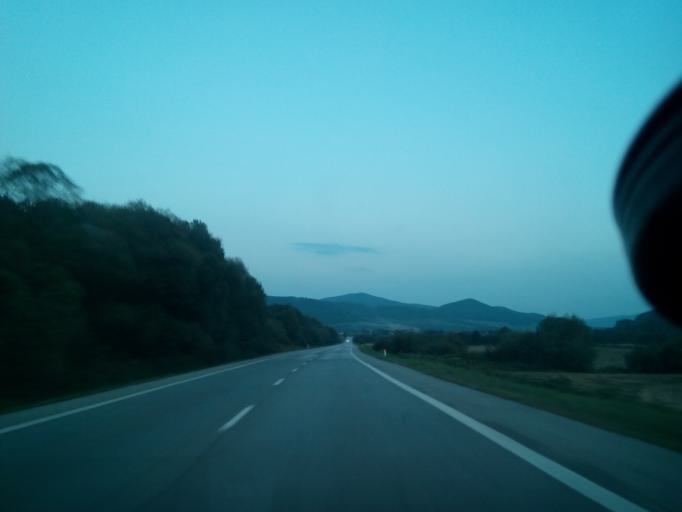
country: SK
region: Kosicky
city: Roznava
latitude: 48.7077
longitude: 20.4890
